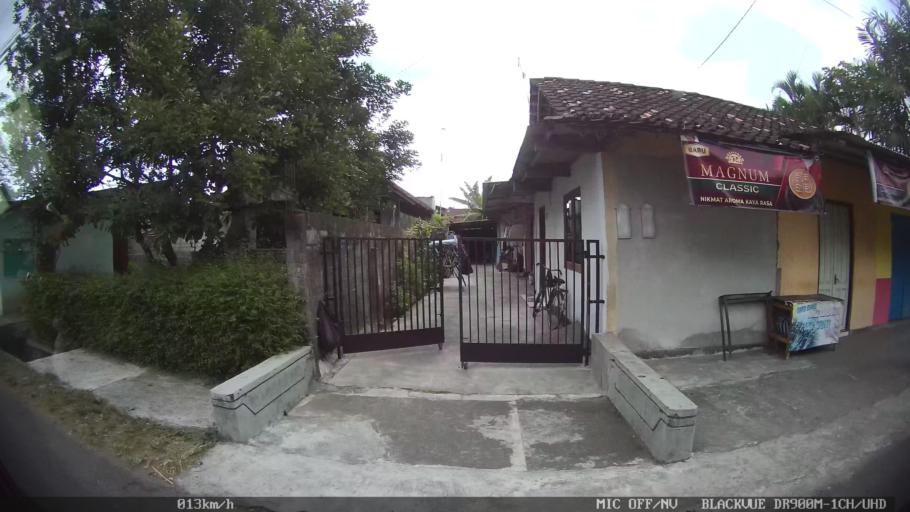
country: ID
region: Daerah Istimewa Yogyakarta
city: Yogyakarta
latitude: -7.7695
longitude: 110.3387
